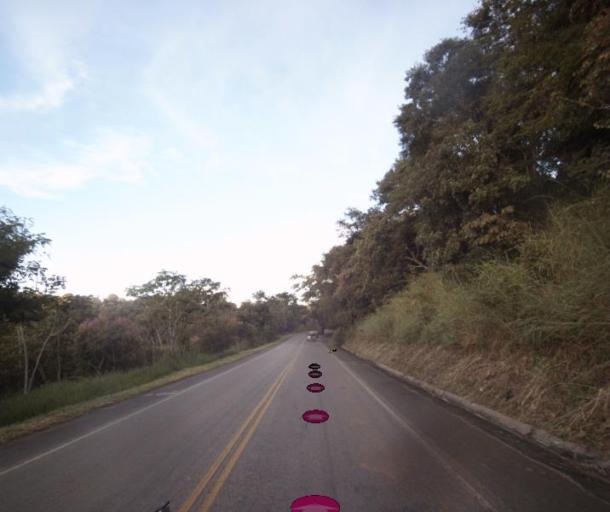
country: BR
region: Goias
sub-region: Abadiania
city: Abadiania
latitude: -16.1114
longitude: -48.8837
